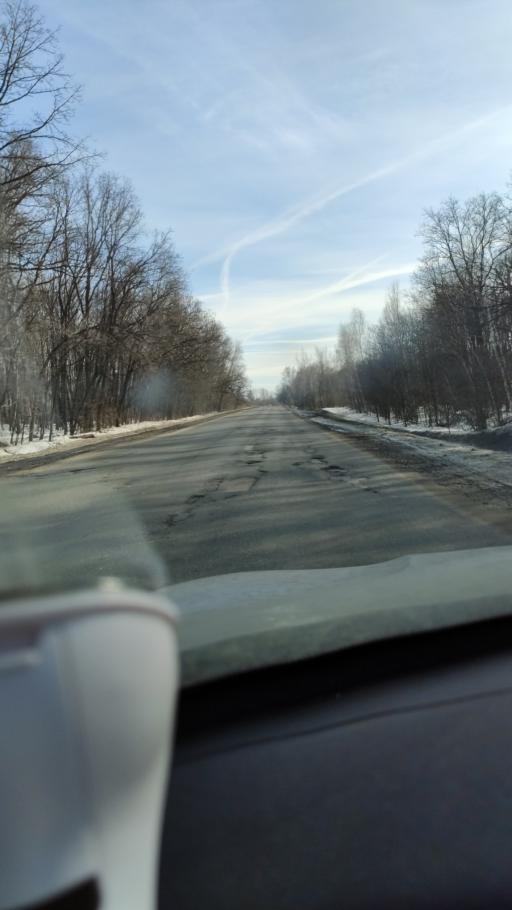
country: RU
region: Samara
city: Novokuybyshevsk
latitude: 52.9785
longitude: 49.8832
